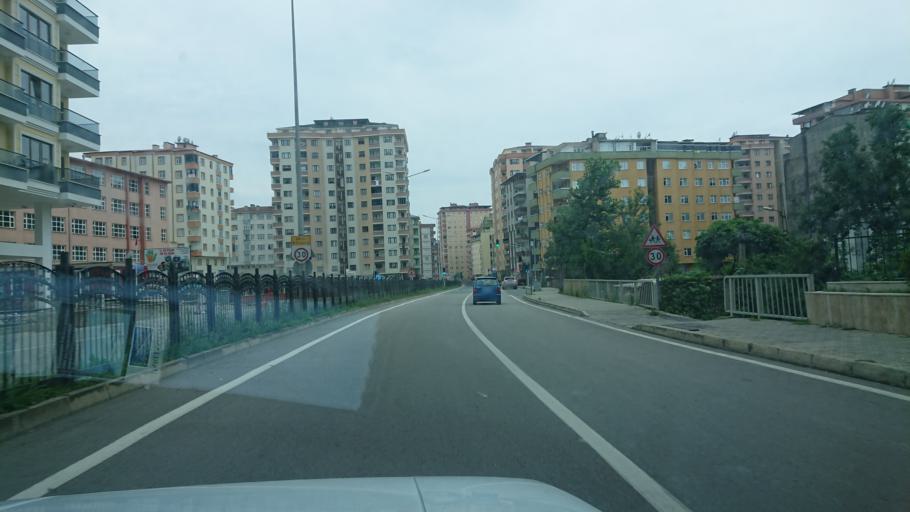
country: TR
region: Rize
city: Rize
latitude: 41.0240
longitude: 40.5431
